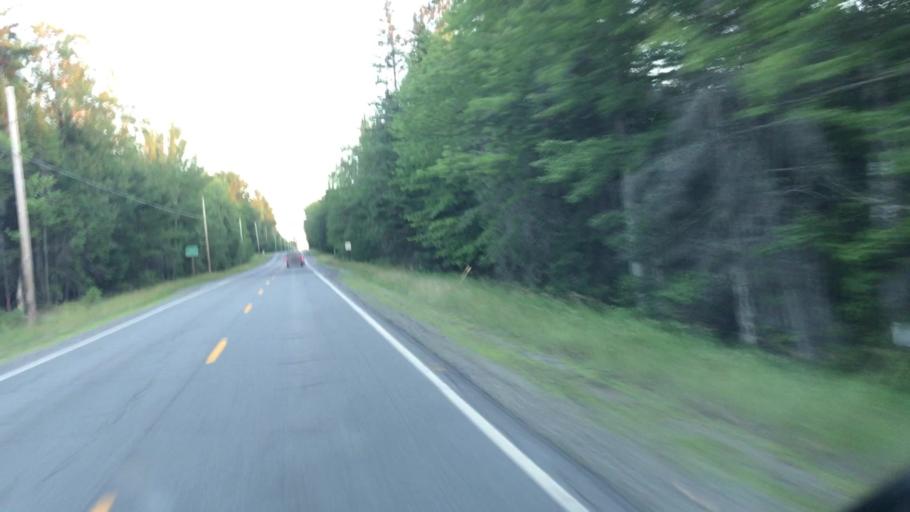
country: US
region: Maine
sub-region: Penobscot County
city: Medway
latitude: 45.5888
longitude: -68.3139
